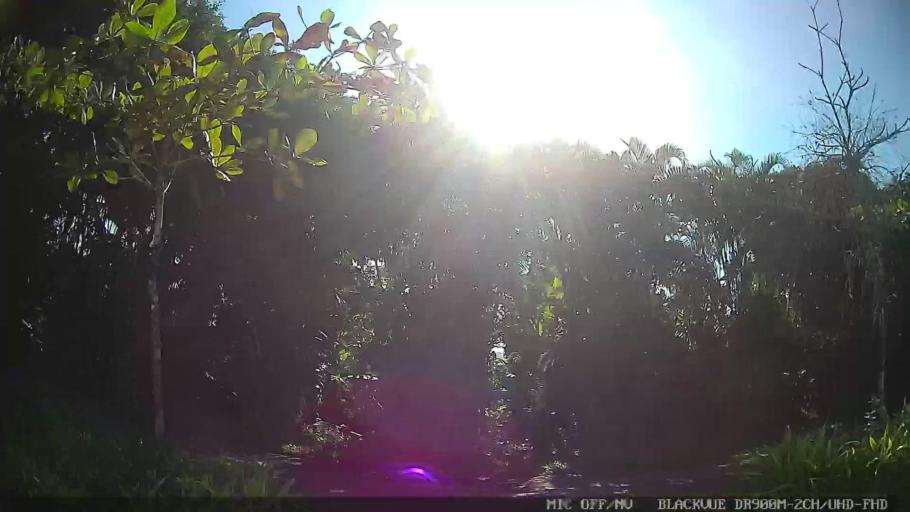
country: BR
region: Sao Paulo
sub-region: Guaruja
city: Guaruja
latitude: -24.0074
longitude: -46.2768
